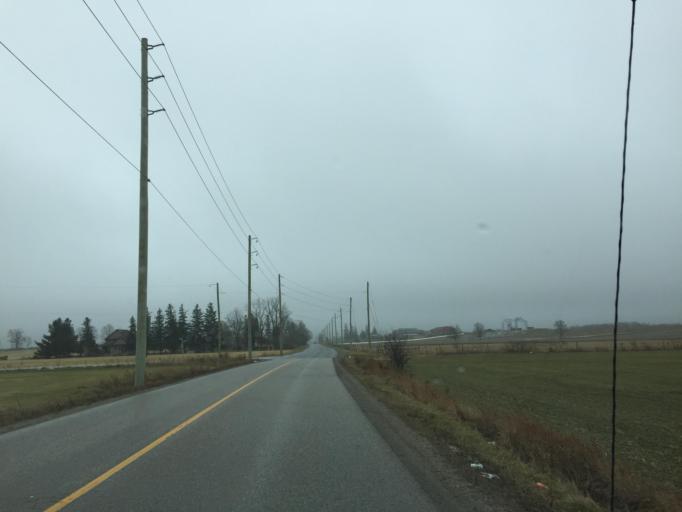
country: CA
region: Ontario
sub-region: Wellington County
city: Guelph
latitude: 43.4858
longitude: -80.3393
